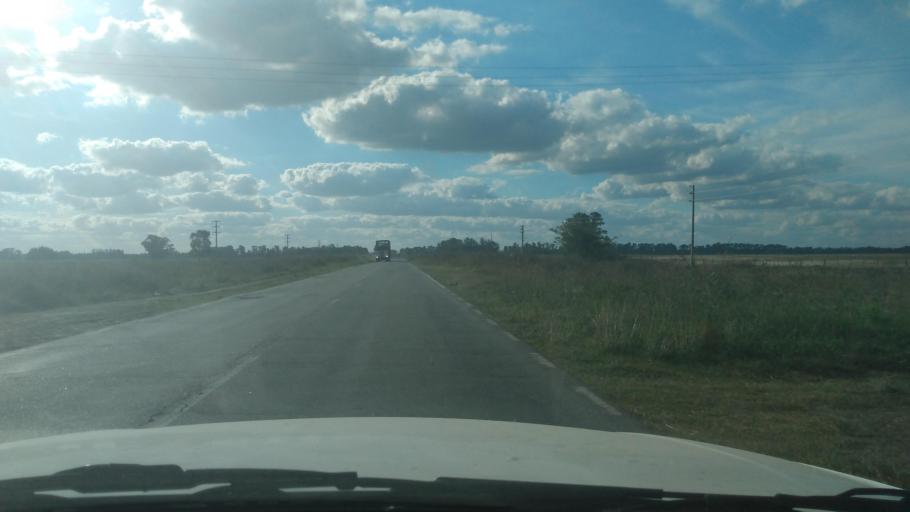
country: AR
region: Buenos Aires
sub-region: Partido de Mercedes
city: Mercedes
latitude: -34.7324
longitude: -59.3892
